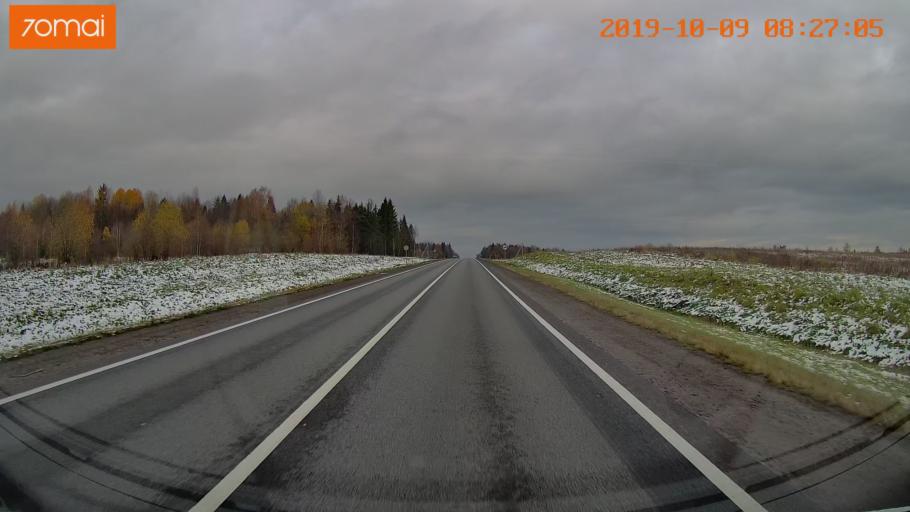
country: RU
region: Vologda
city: Gryazovets
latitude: 58.7995
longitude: 40.2546
